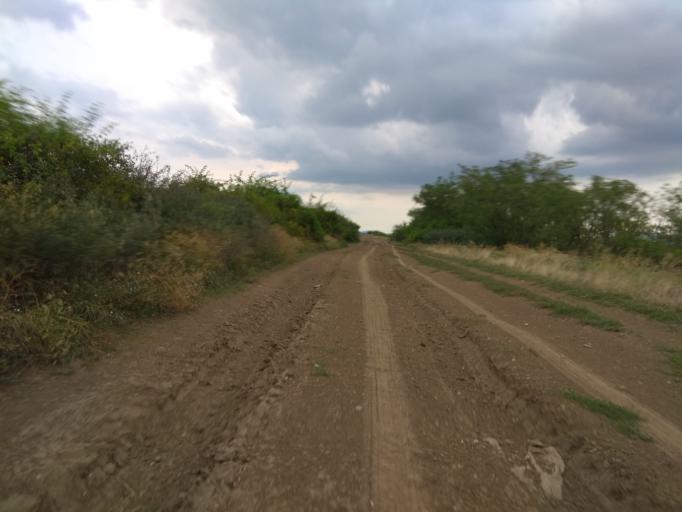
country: HU
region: Borsod-Abauj-Zemplen
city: Megyaszo
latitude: 48.1528
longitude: 21.1094
